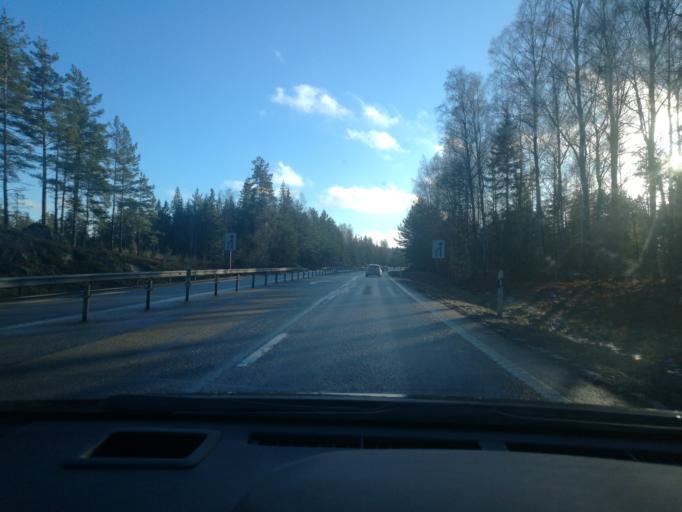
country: SE
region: OEstergoetland
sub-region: Norrkopings Kommun
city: Jursla
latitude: 58.7305
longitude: 16.1733
